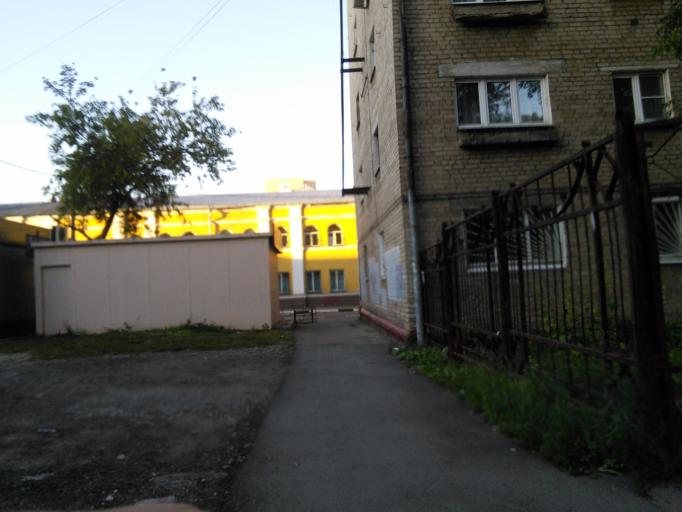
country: RU
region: Moskovskaya
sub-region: Podol'skiy Rayon
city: Podol'sk
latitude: 55.4314
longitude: 37.5493
